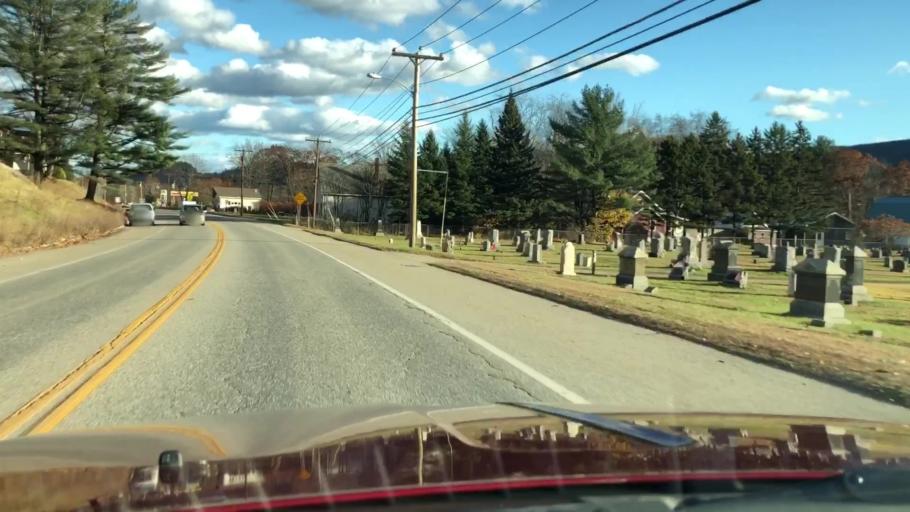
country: US
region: Maine
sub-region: Oxford County
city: Mexico
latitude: 44.5368
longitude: -70.5122
